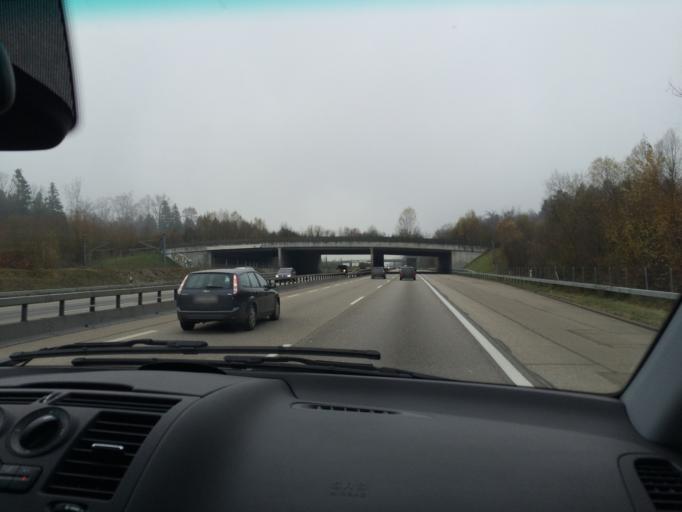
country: CH
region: Bern
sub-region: Emmental District
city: Koppigen
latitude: 47.1261
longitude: 7.5821
